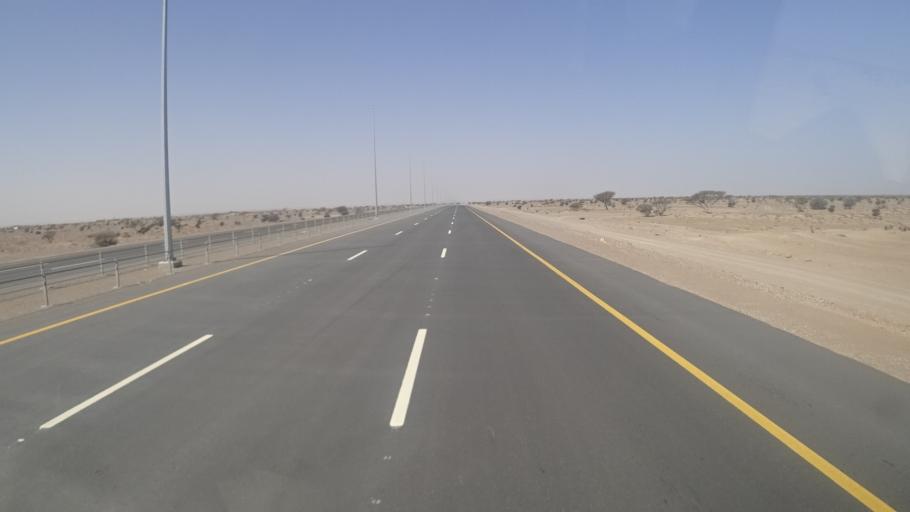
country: OM
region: Ash Sharqiyah
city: Sur
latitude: 22.2742
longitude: 59.2170
